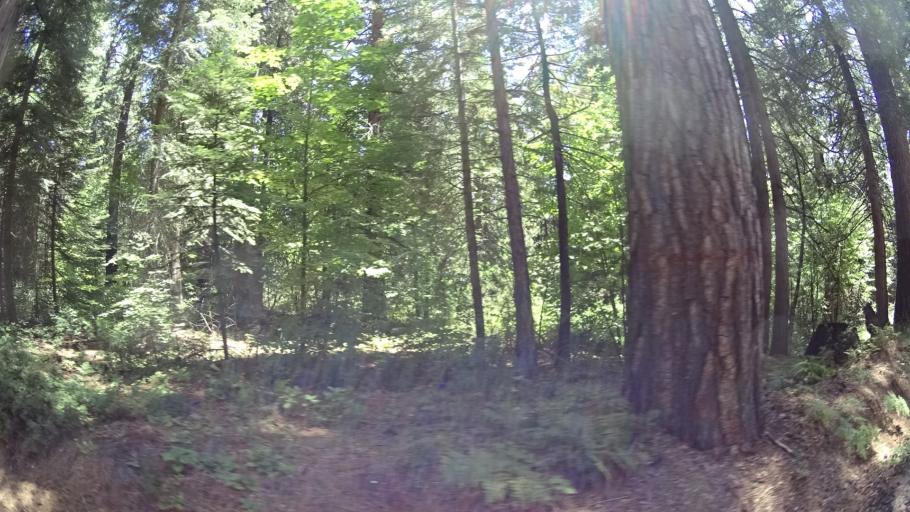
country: US
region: California
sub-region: Calaveras County
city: Arnold
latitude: 38.2505
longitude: -120.3055
